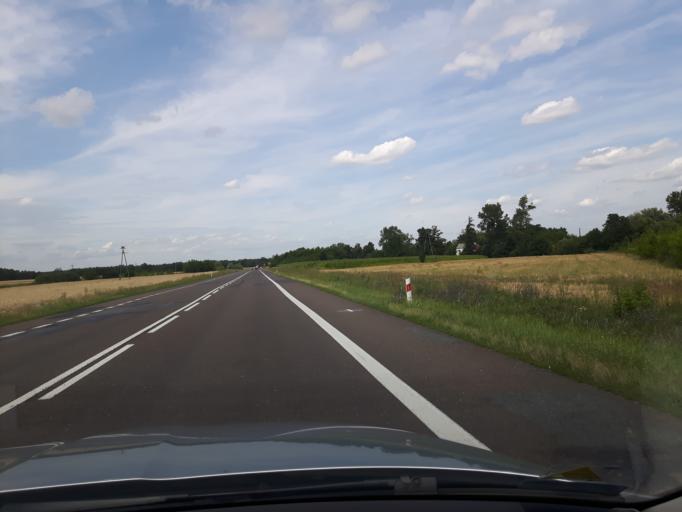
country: PL
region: Masovian Voivodeship
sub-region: Powiat ciechanowski
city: Glinojeck
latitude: 52.7942
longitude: 20.2721
